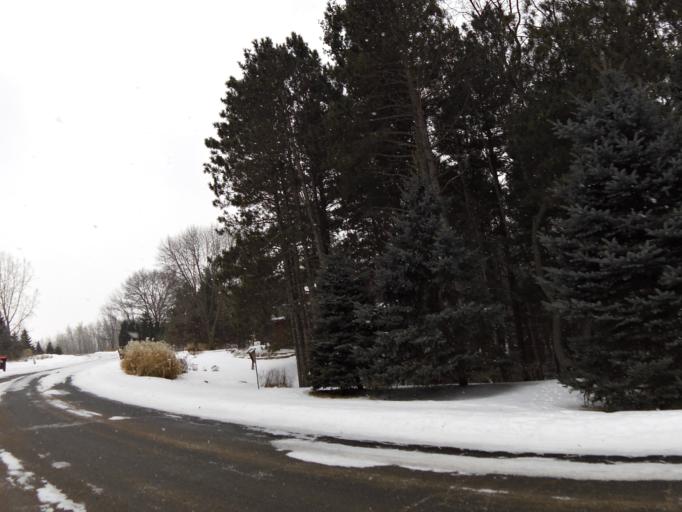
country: US
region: Minnesota
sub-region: Washington County
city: Lake Elmo
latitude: 44.9718
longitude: -92.8416
